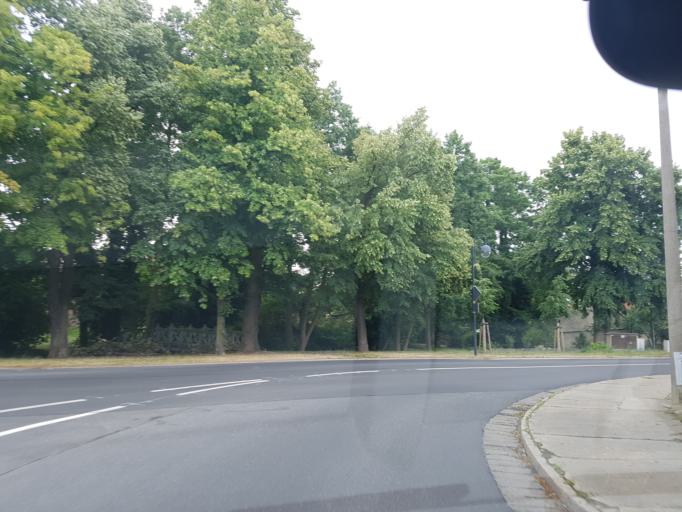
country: DE
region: Brandenburg
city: Luckau
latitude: 51.8530
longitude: 13.7092
